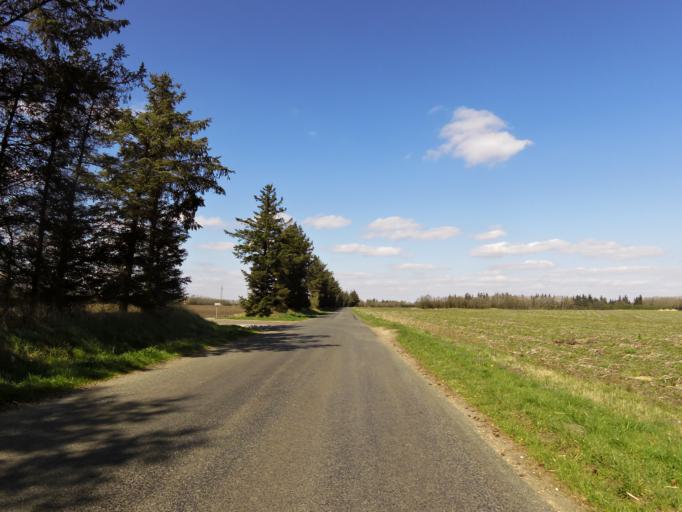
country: DK
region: South Denmark
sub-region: Esbjerg Kommune
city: Ribe
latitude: 55.3363
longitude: 8.8329
